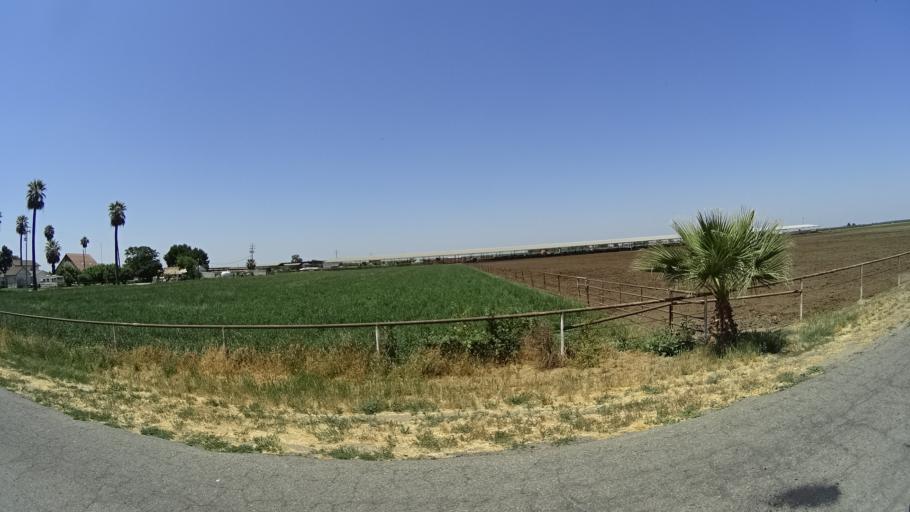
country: US
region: California
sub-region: Kings County
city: Armona
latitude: 36.3597
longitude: -119.7269
